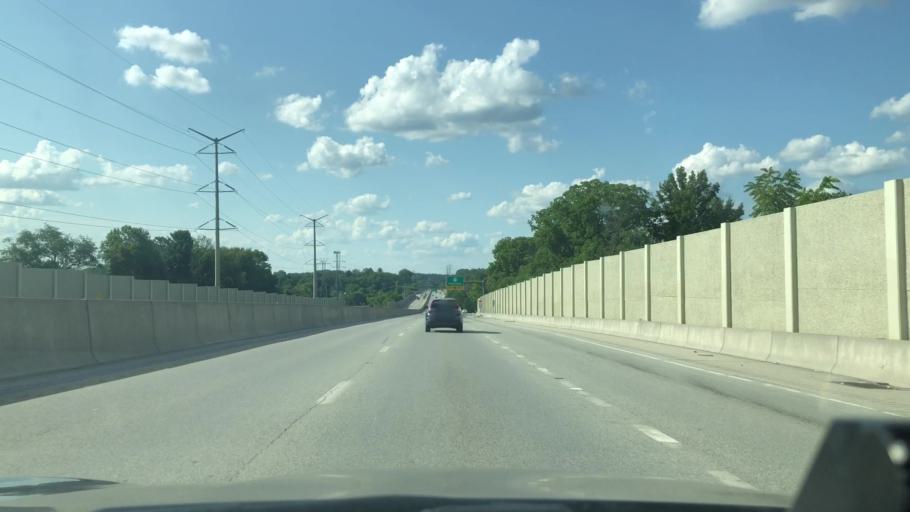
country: US
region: Pennsylvania
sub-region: Montgomery County
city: Flourtown
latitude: 40.1081
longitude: -75.1986
